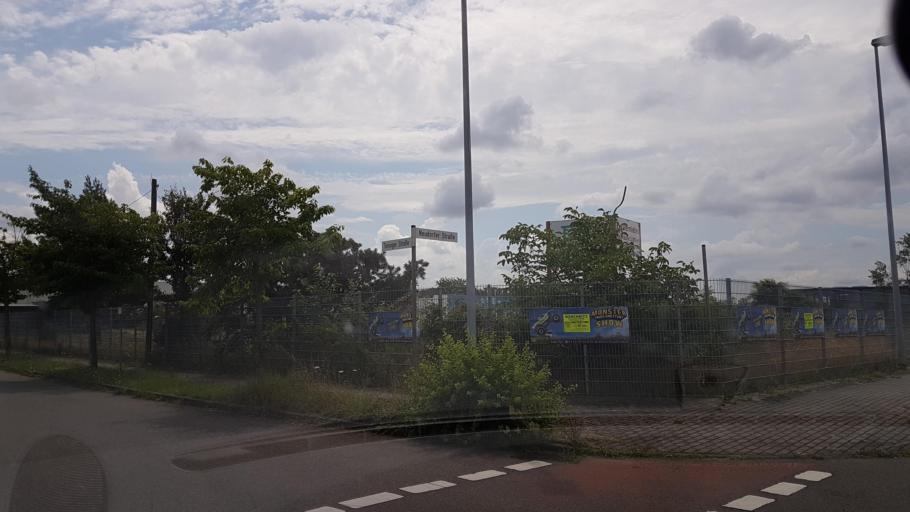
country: DE
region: Saxony
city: Zeithain
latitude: 51.3407
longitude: 13.3420
